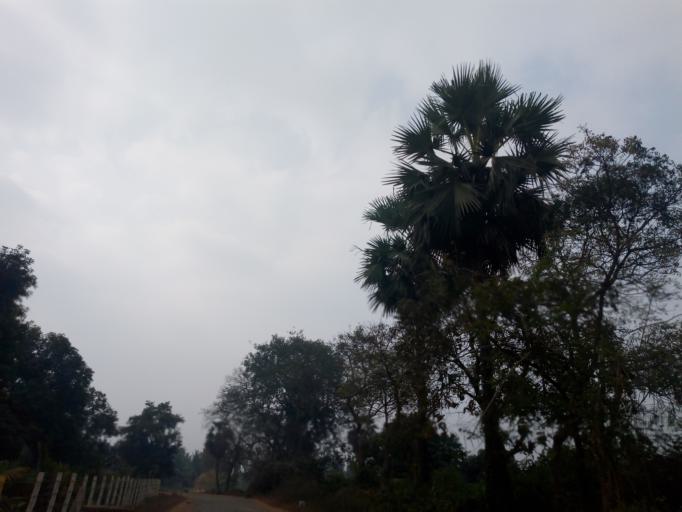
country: IN
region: Andhra Pradesh
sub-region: West Godavari
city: Tadepallegudem
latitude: 16.8644
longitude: 81.3254
